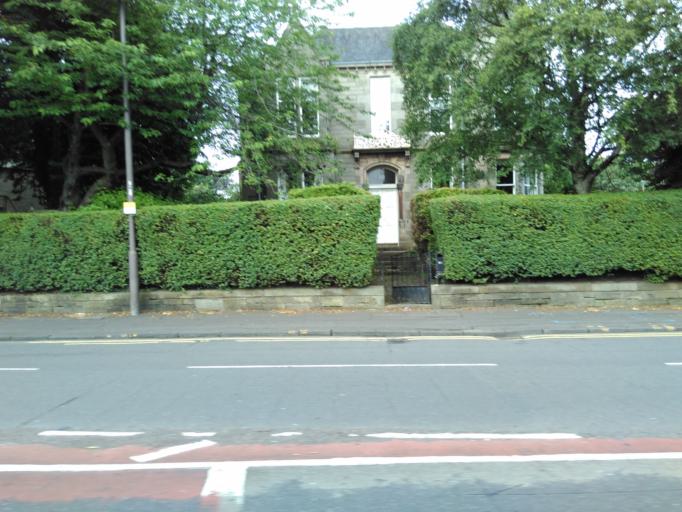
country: GB
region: Scotland
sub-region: Edinburgh
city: Edinburgh
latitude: 55.9268
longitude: -3.1671
